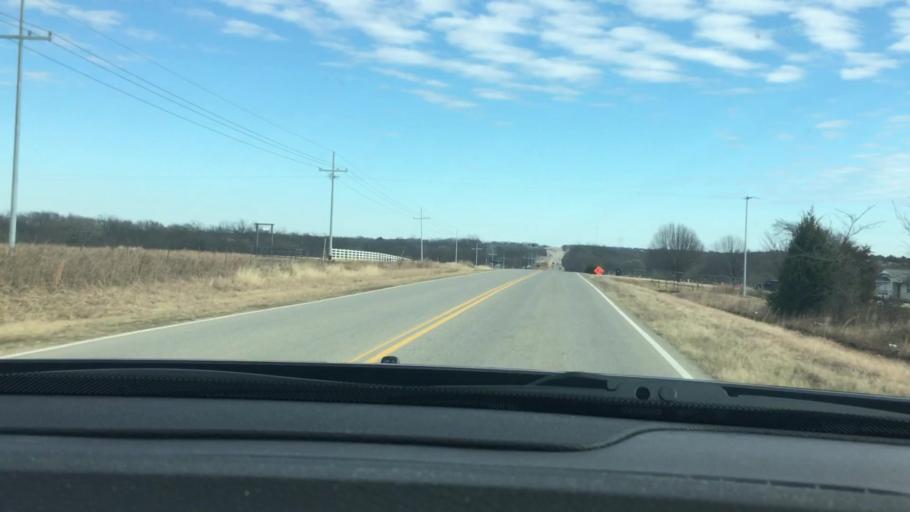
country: US
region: Oklahoma
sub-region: Garvin County
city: Stratford
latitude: 34.7967
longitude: -96.8809
